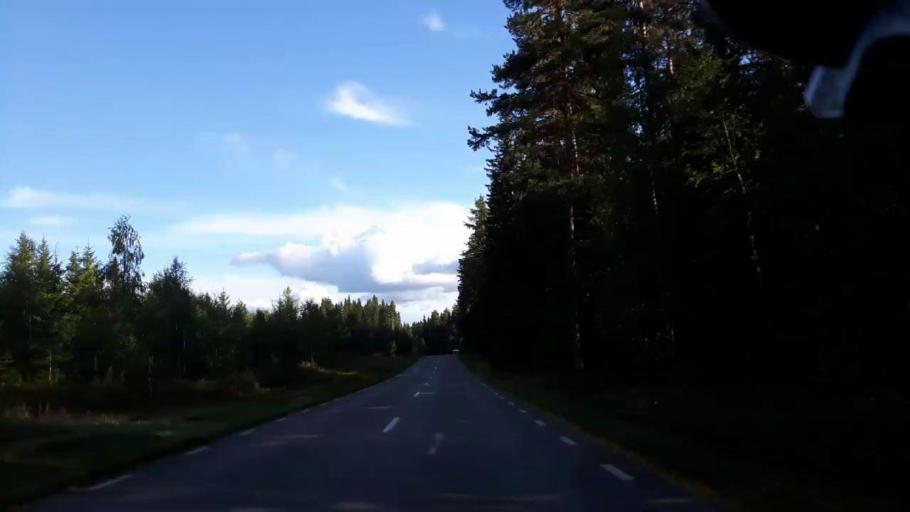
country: SE
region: Jaemtland
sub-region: Stroemsunds Kommun
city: Stroemsund
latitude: 63.3987
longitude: 15.5735
